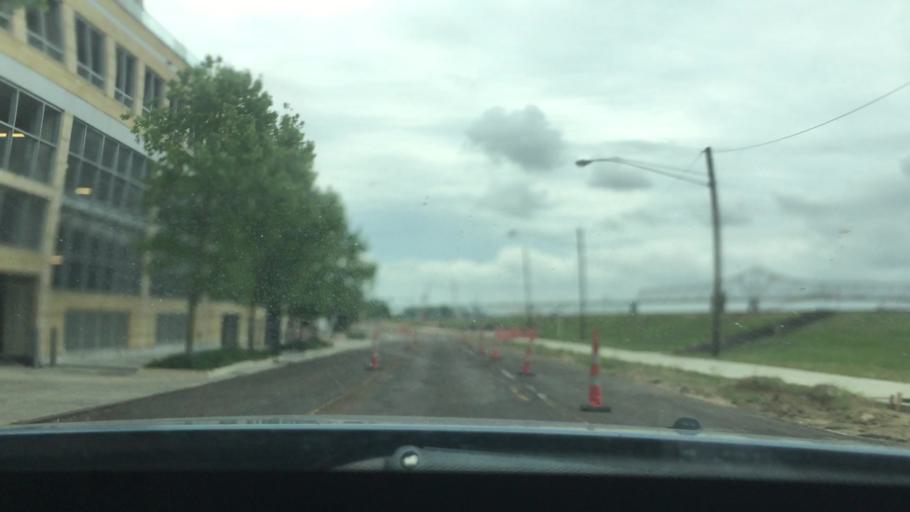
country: US
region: Louisiana
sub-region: West Baton Rouge Parish
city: Port Allen
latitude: 30.4521
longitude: -91.1905
